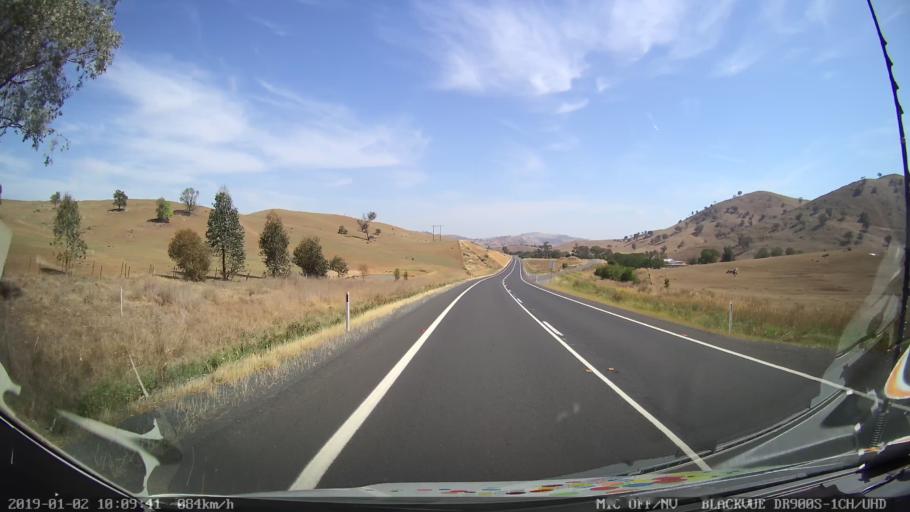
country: AU
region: New South Wales
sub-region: Gundagai
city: Gundagai
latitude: -35.1139
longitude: 148.0979
